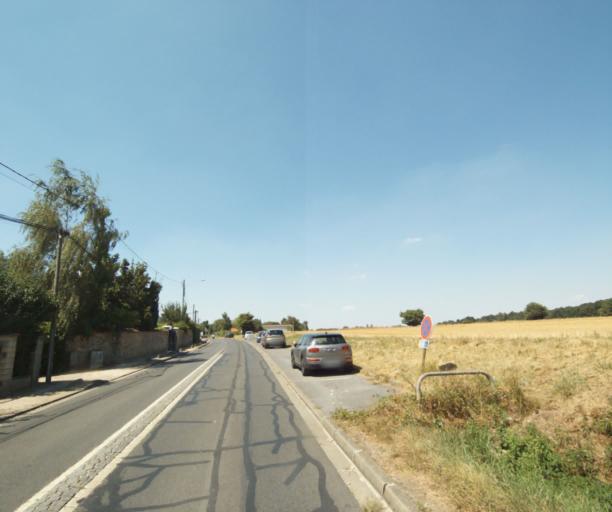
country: FR
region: Ile-de-France
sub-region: Departement de Seine-et-Marne
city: Conches-sur-Gondoire
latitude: 48.8609
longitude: 2.7242
